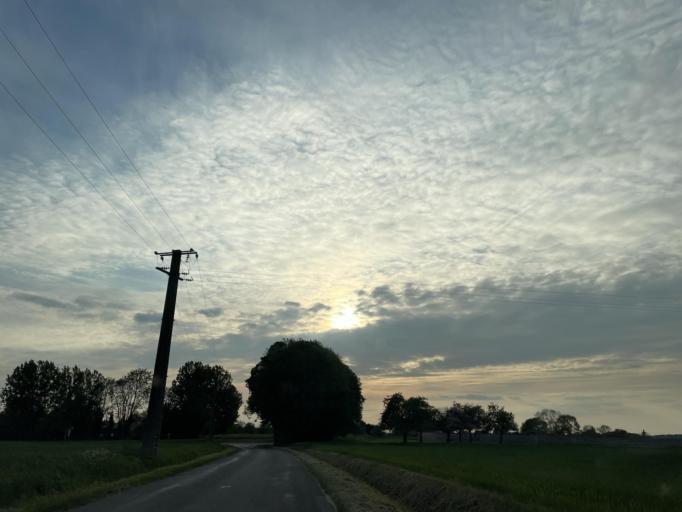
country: FR
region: Ile-de-France
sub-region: Departement de Seine-et-Marne
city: Bouleurs
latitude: 48.8920
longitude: 2.9371
